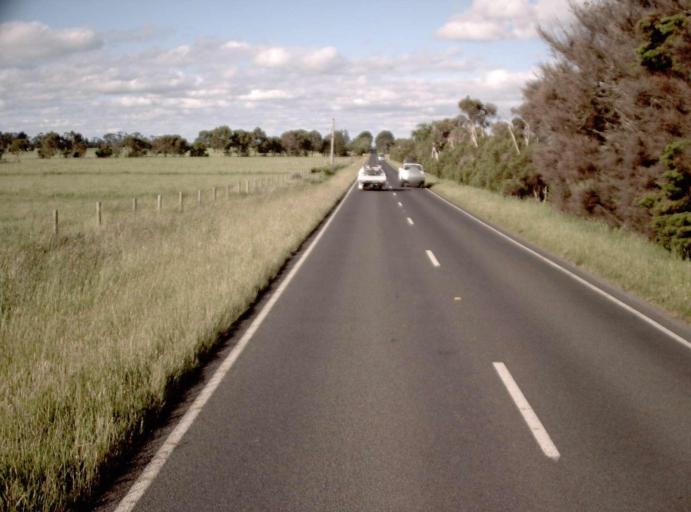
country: AU
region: Victoria
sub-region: Bass Coast
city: North Wonthaggi
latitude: -38.5192
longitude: 145.8949
